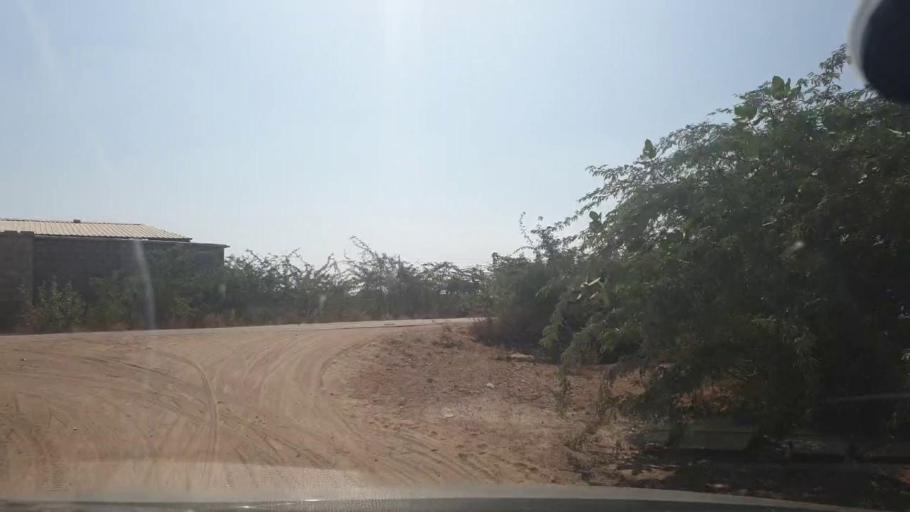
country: PK
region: Sindh
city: Malir Cantonment
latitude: 25.1665
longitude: 67.2044
